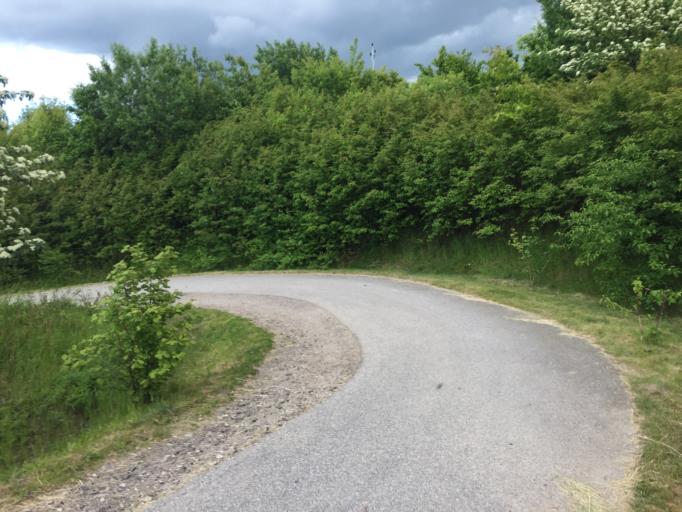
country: SE
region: Skane
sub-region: Lunds Kommun
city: Lund
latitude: 55.7440
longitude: 13.1936
